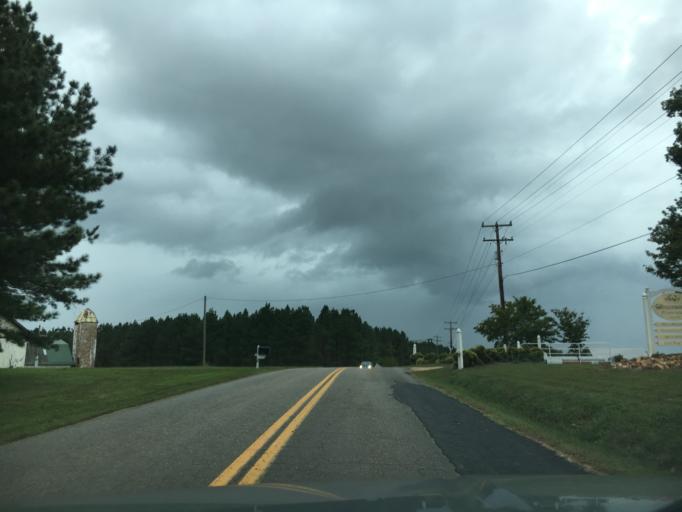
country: US
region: Virginia
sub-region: Amelia County
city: Amelia Court House
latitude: 37.3790
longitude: -77.9778
